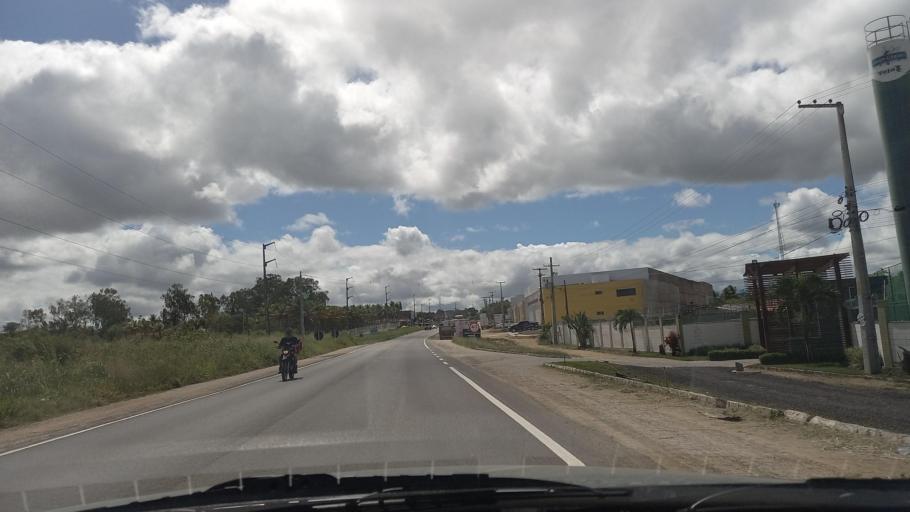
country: BR
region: Pernambuco
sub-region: Caruaru
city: Caruaru
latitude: -8.2562
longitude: -35.9526
